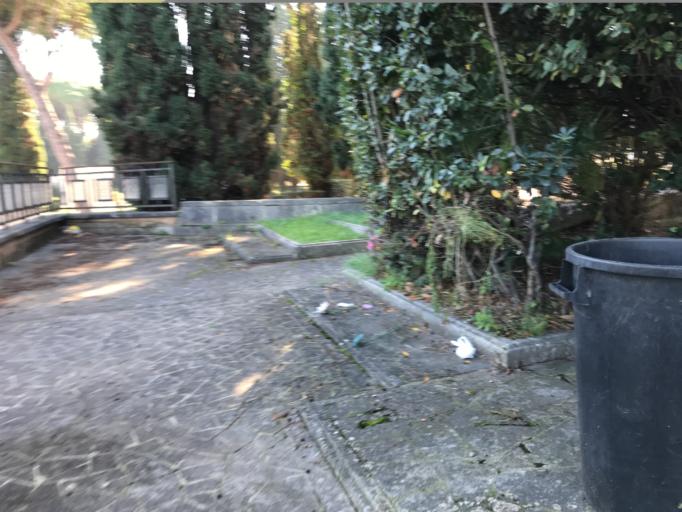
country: IT
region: Latium
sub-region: Citta metropolitana di Roma Capitale
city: Rome
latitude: 41.8999
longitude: 12.5243
